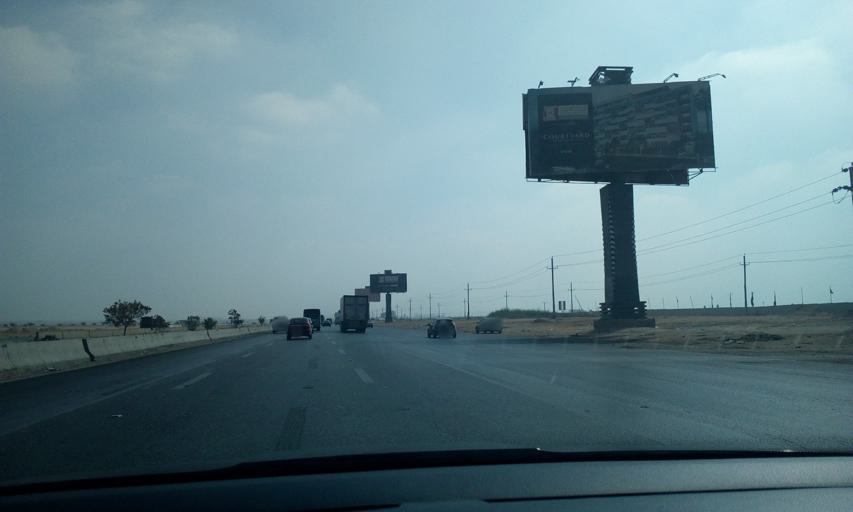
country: EG
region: Eastern Province
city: Bilbays
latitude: 30.2022
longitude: 31.6643
